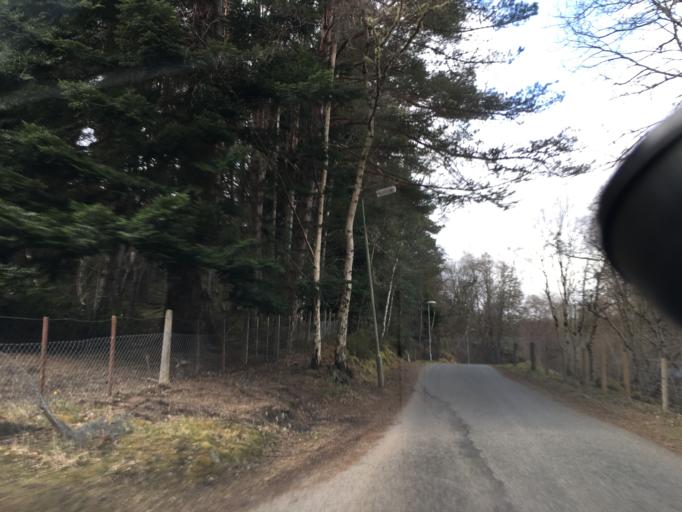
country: GB
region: Scotland
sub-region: Highland
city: Kingussie
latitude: 57.0849
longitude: -4.0563
